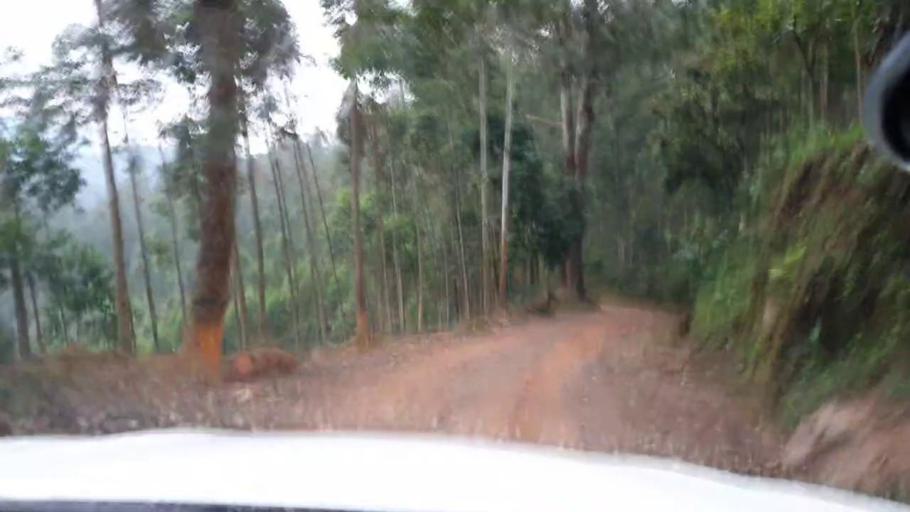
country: RW
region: Western Province
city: Cyangugu
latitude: -2.4090
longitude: 29.2005
